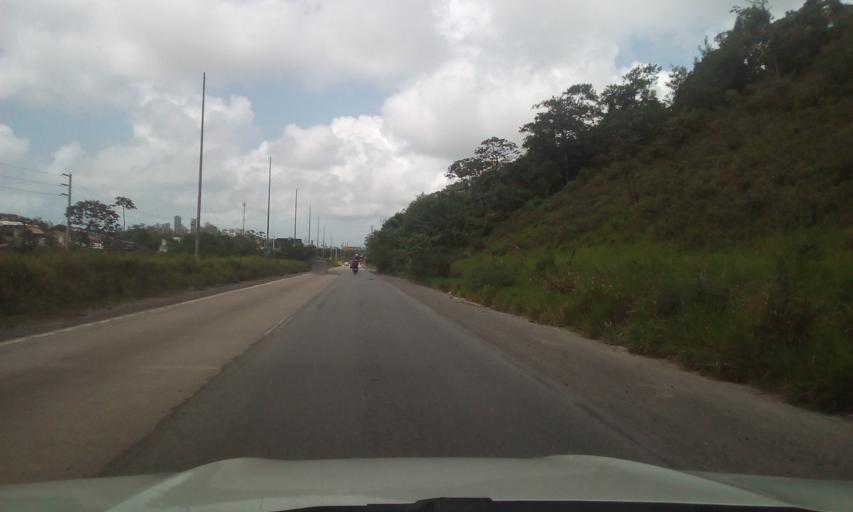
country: BR
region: Pernambuco
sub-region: Recife
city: Recife
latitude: -8.0017
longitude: -34.9387
